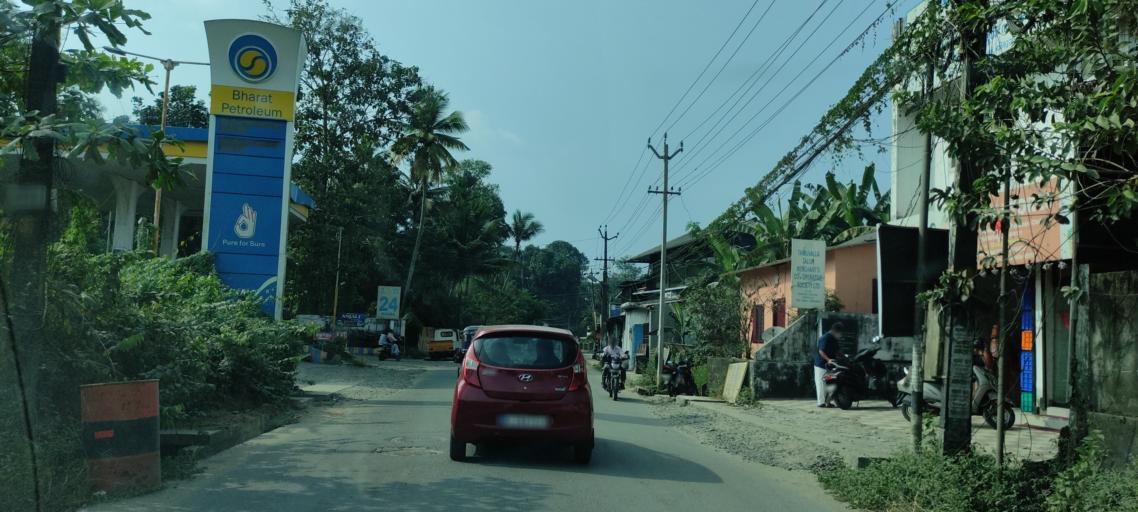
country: IN
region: Kerala
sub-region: Pattanamtitta
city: Tiruvalla
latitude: 9.3789
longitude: 76.5634
